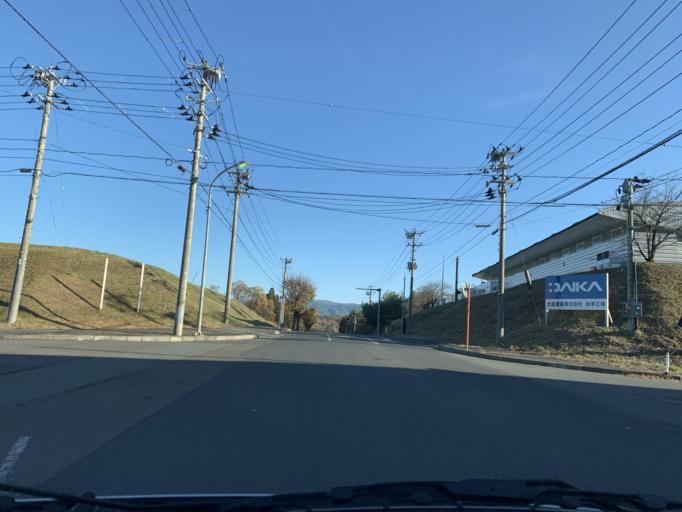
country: JP
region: Iwate
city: Mizusawa
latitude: 39.2067
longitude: 141.1823
